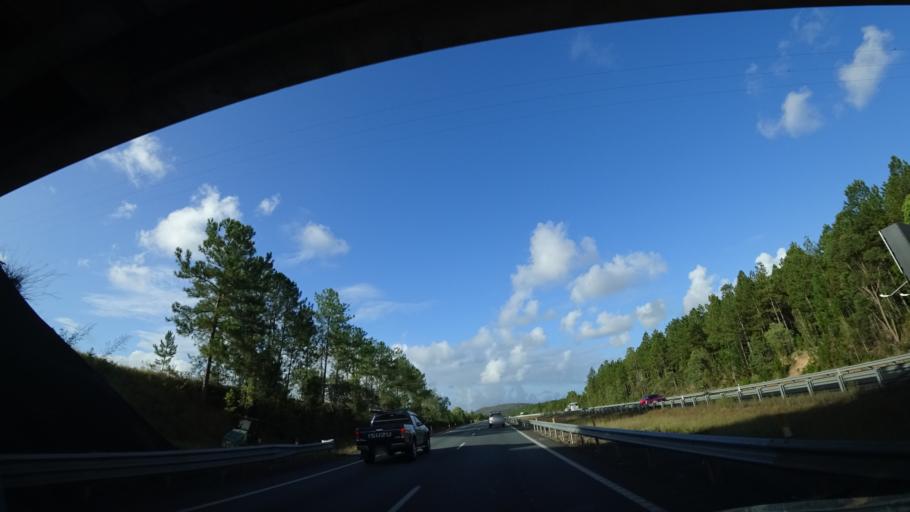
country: AU
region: Queensland
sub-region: Moreton Bay
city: Caboolture
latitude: -26.9577
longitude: 152.9872
